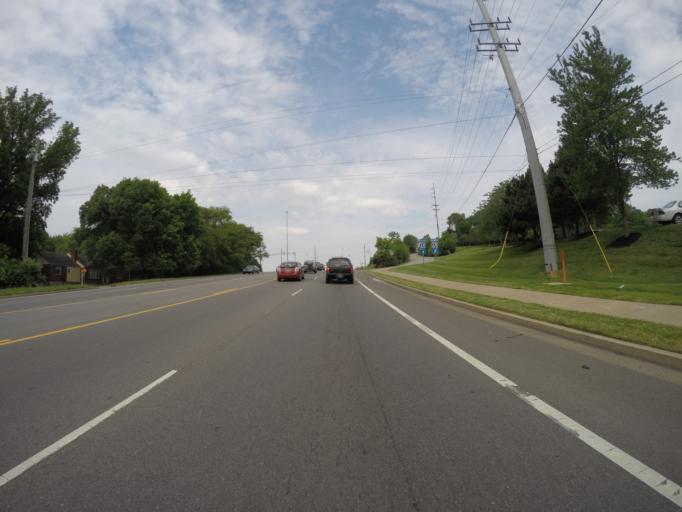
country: US
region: Tennessee
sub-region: Davidson County
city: Goodlettsville
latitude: 36.2643
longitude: -86.7346
